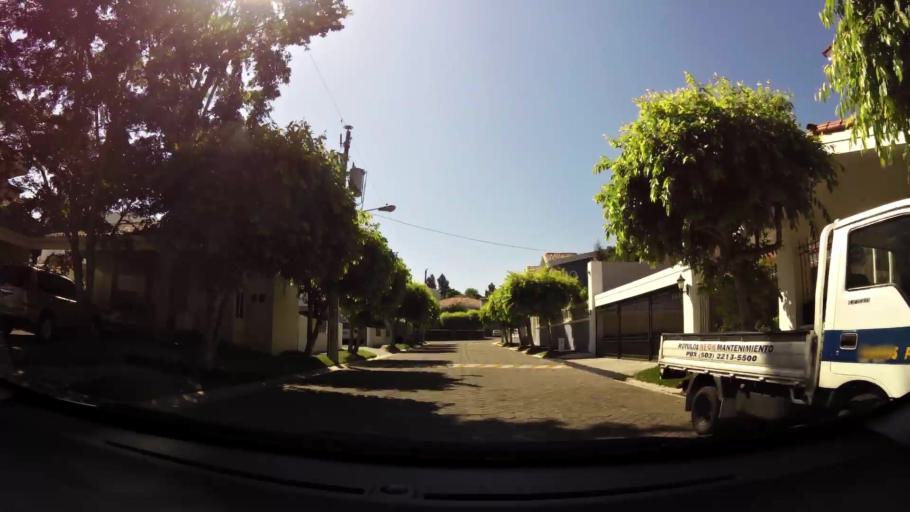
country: SV
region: La Libertad
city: Nuevo Cuscatlan
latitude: 13.6567
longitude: -89.2802
